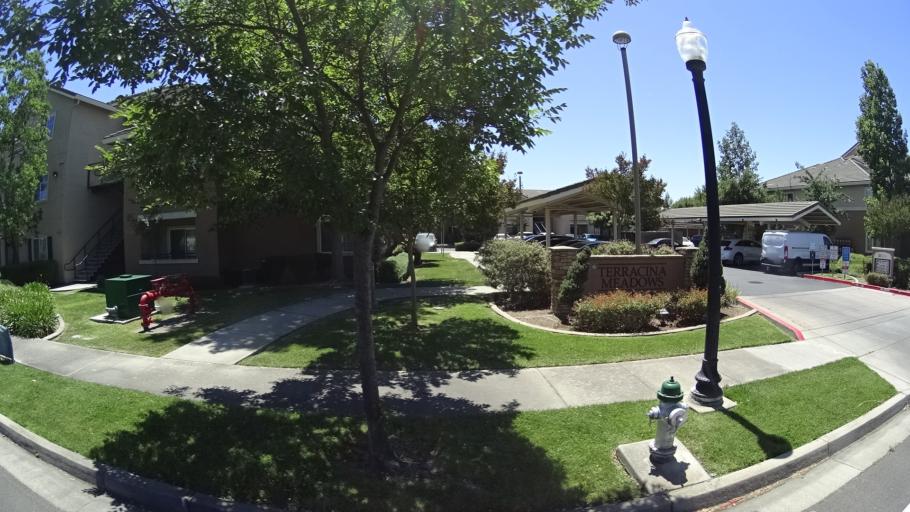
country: US
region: California
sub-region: Yolo County
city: West Sacramento
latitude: 38.6543
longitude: -121.5362
